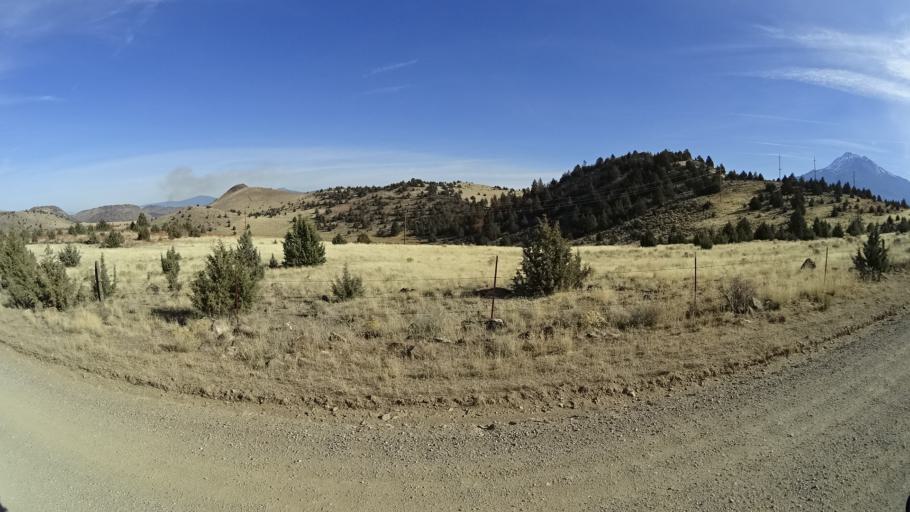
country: US
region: California
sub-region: Siskiyou County
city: Weed
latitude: 41.4919
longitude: -122.4514
